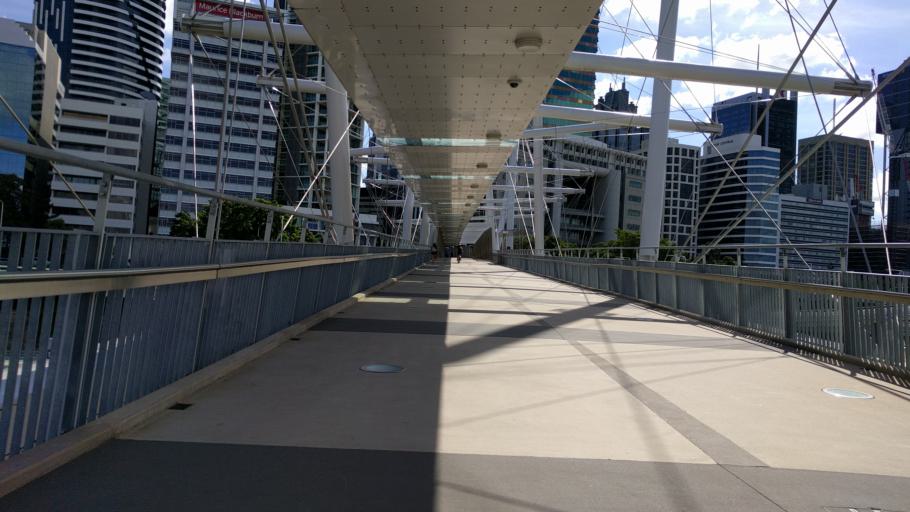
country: AU
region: Queensland
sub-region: Brisbane
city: Spring Hill
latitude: -27.4695
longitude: 153.0178
